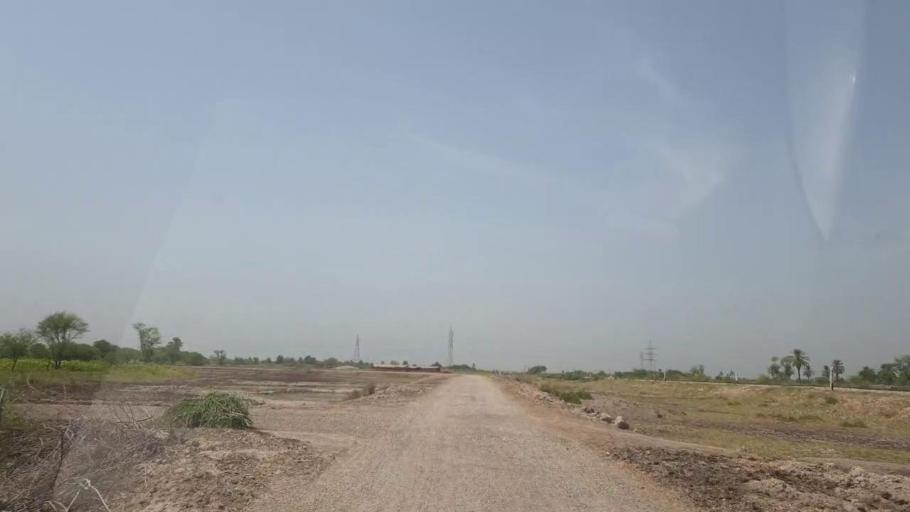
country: PK
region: Sindh
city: Gambat
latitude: 27.3178
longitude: 68.5352
